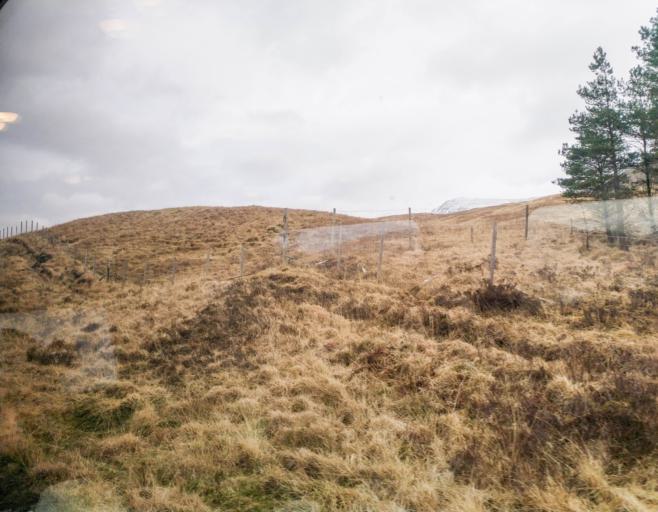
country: GB
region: Scotland
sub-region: Highland
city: Spean Bridge
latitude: 56.5356
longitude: -4.7625
